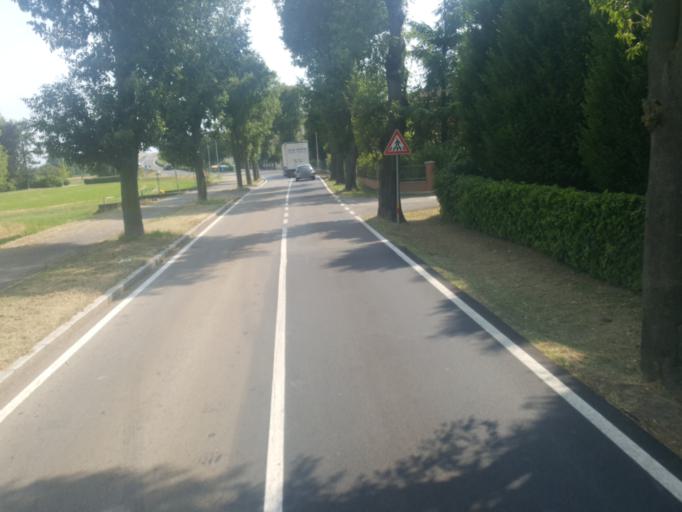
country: IT
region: Emilia-Romagna
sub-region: Provincia di Modena
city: Gaggio
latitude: 44.6288
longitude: 11.0090
